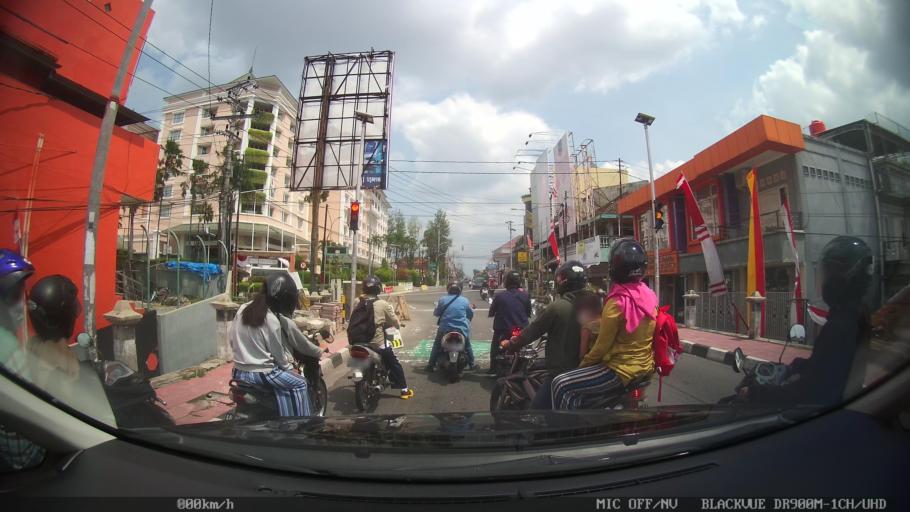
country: ID
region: Daerah Istimewa Yogyakarta
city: Yogyakarta
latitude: -7.7967
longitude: 110.3695
